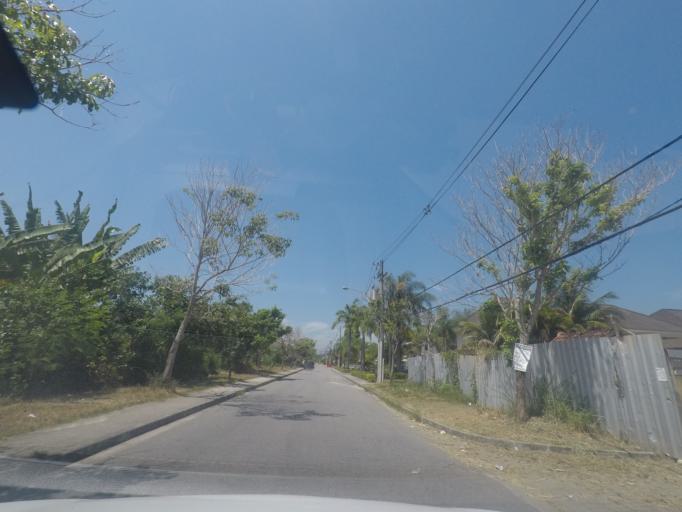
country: BR
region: Rio de Janeiro
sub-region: Nilopolis
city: Nilopolis
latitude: -22.9869
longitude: -43.4604
